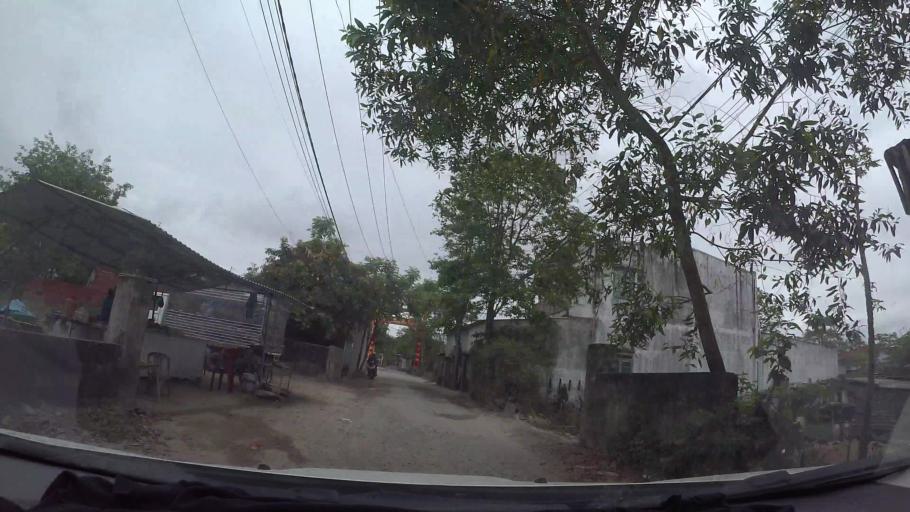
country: VN
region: Da Nang
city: Lien Chieu
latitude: 16.0857
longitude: 108.1029
